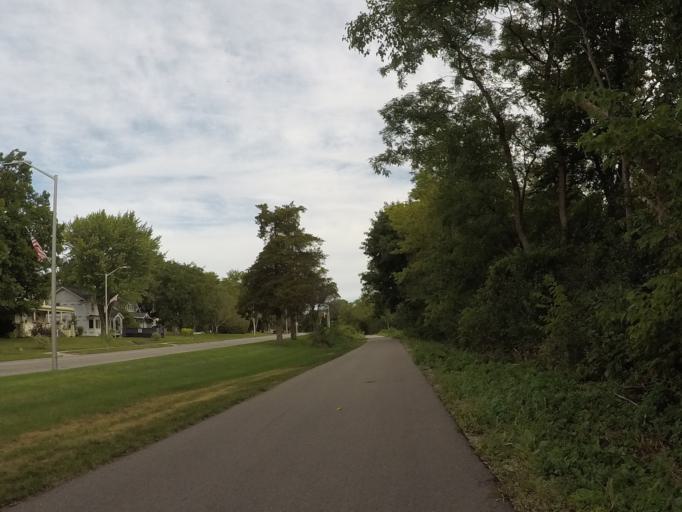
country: US
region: Wisconsin
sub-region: Sauk County
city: Prairie du Sac
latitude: 43.2841
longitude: -89.7178
